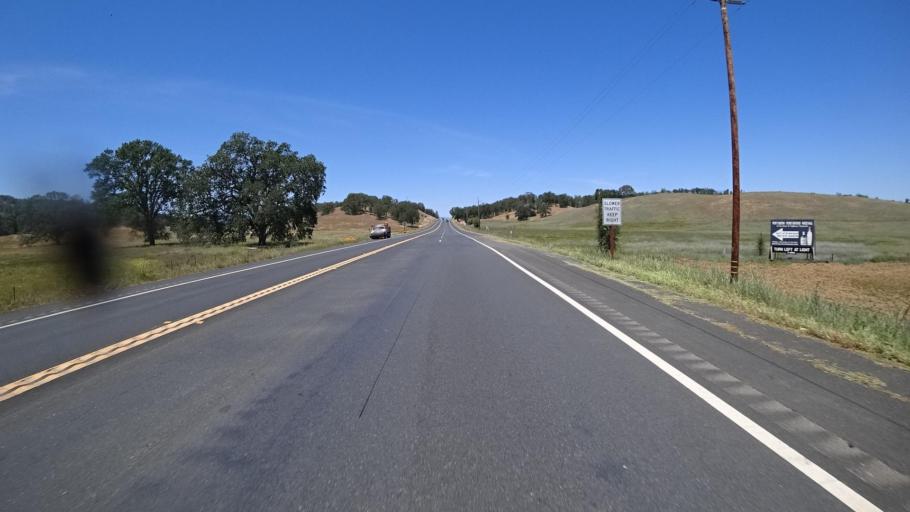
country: US
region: California
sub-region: Lake County
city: Lower Lake
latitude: 38.8954
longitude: -122.6079
